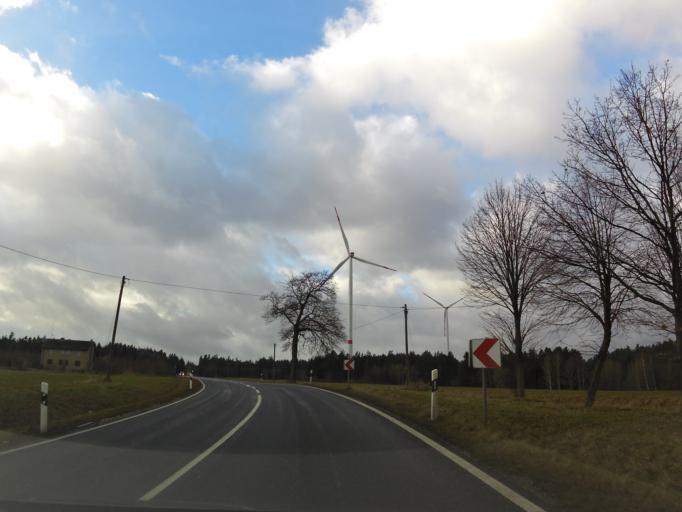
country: DE
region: Bavaria
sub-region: Upper Franconia
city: Hochstadt bei Thiersheim
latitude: 50.0741
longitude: 12.0953
